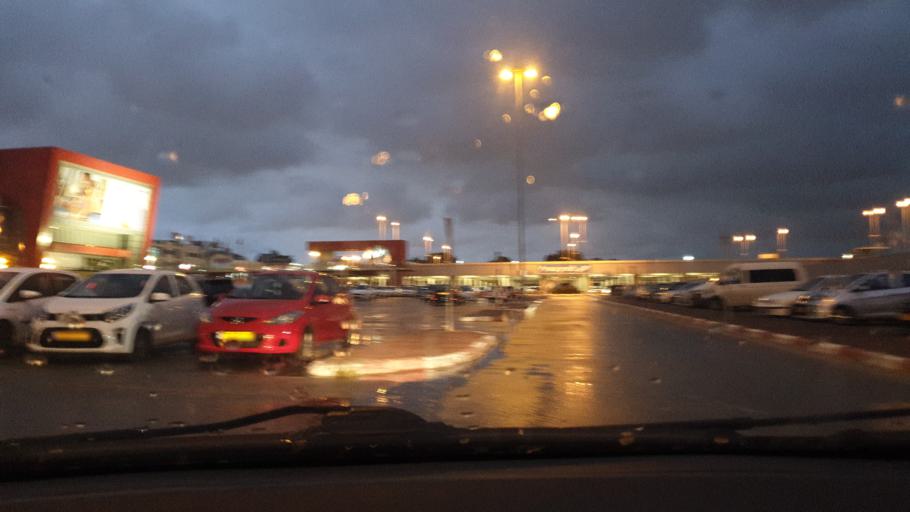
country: IL
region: Tel Aviv
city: Holon
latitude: 31.9898
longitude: 34.7753
